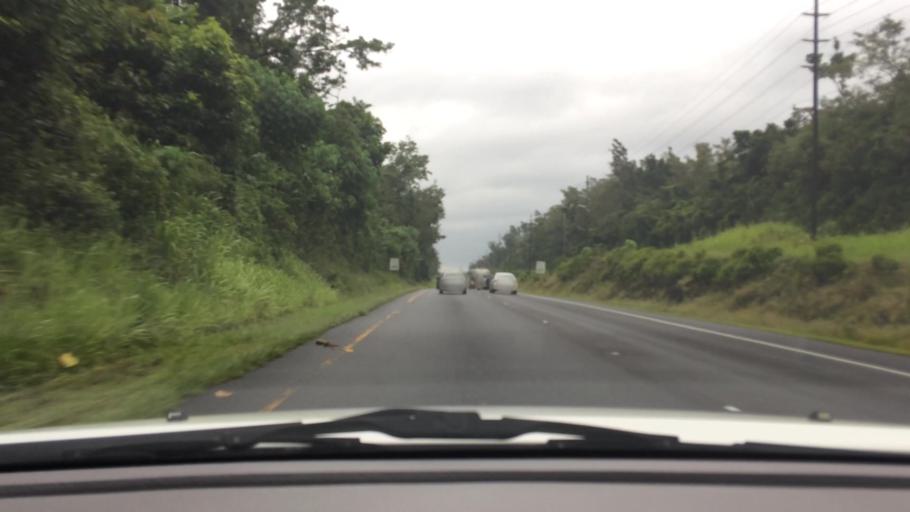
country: US
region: Hawaii
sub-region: Hawaii County
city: Kea'au
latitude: 19.6425
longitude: -155.0463
